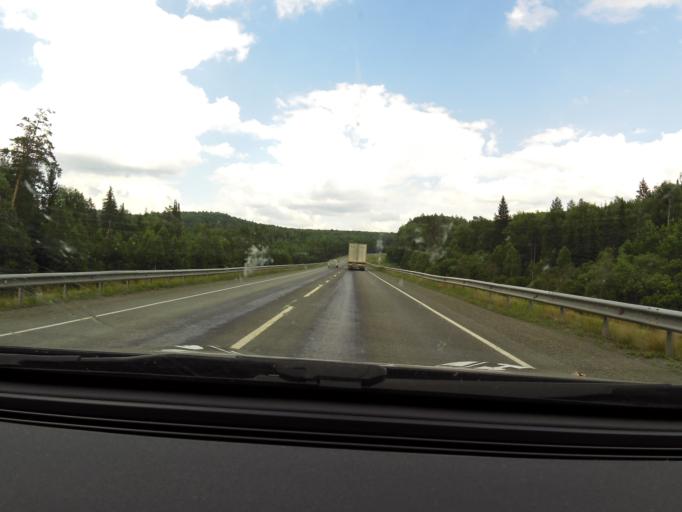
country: RU
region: Sverdlovsk
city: Bisert'
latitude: 56.8377
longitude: 58.8641
